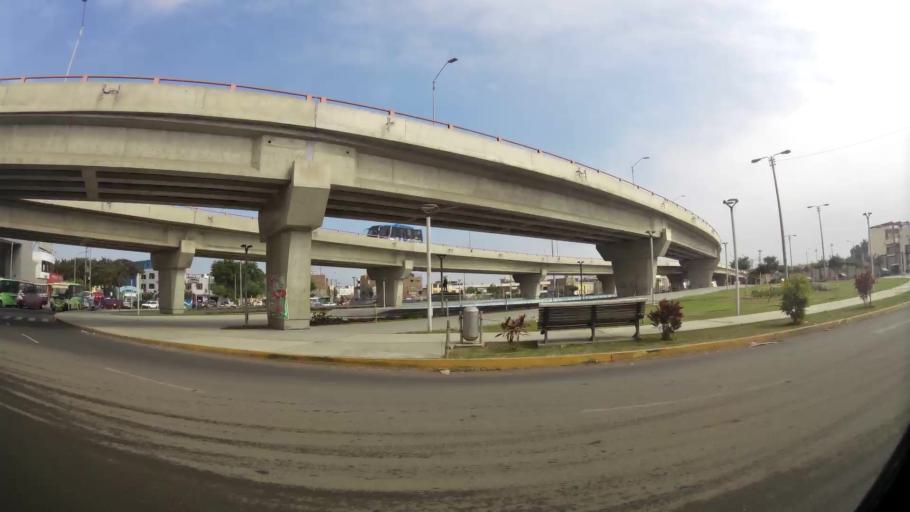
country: PE
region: La Libertad
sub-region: Provincia de Trujillo
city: Trujillo
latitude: -8.1230
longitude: -79.0231
